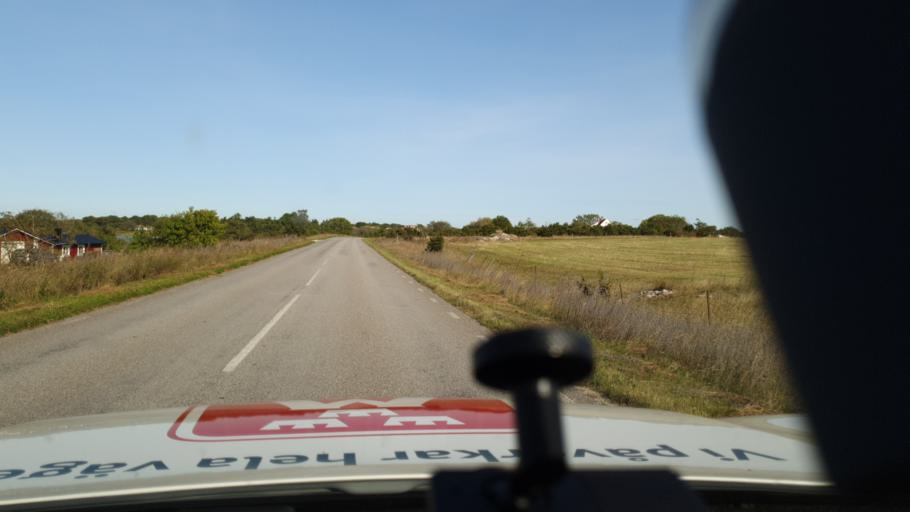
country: SE
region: Gotland
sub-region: Gotland
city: Slite
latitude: 57.9236
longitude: 19.1424
